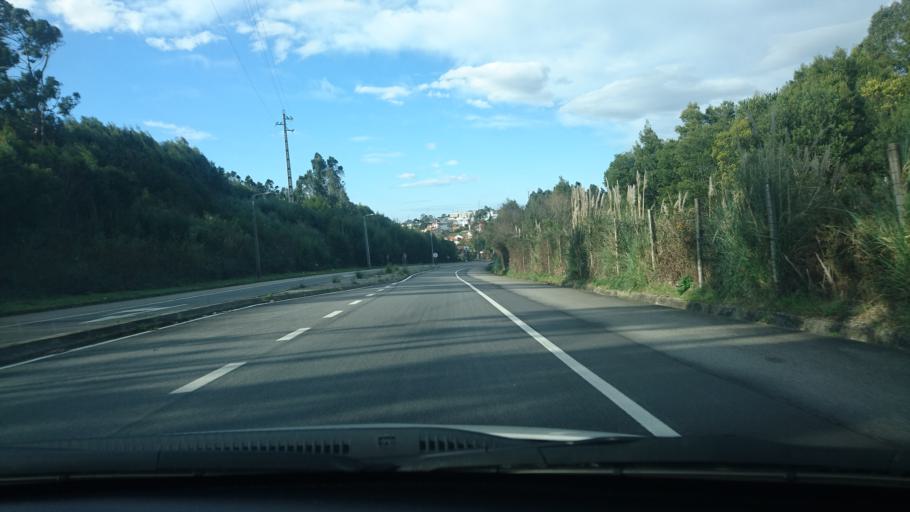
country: PT
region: Aveiro
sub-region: Santa Maria da Feira
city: Rio Meao
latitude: 40.9631
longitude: -8.5911
